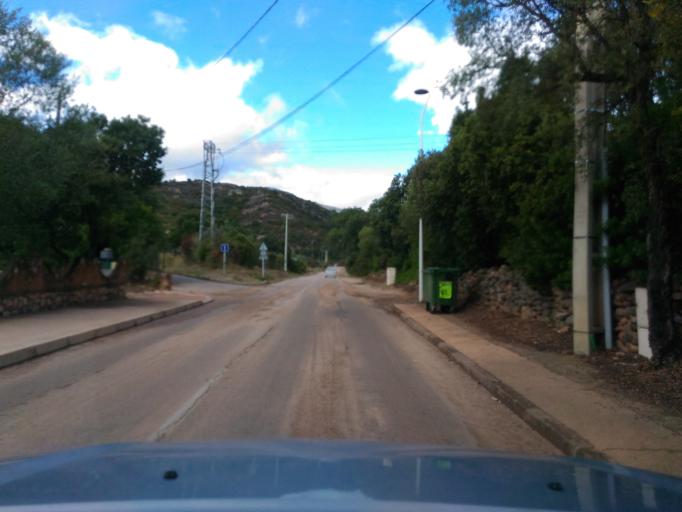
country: FR
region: Corsica
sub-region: Departement de la Corse-du-Sud
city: Porto-Vecchio
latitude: 41.7011
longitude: 9.3404
